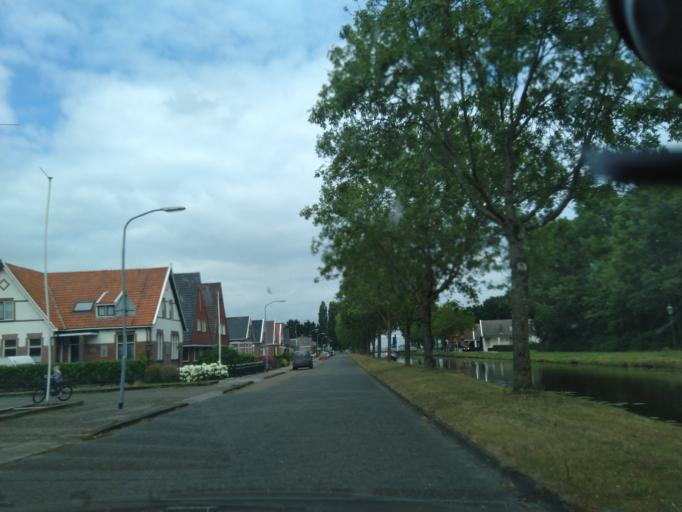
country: NL
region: Groningen
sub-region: Gemeente Pekela
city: Oude Pekela
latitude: 53.1105
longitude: 7.0232
